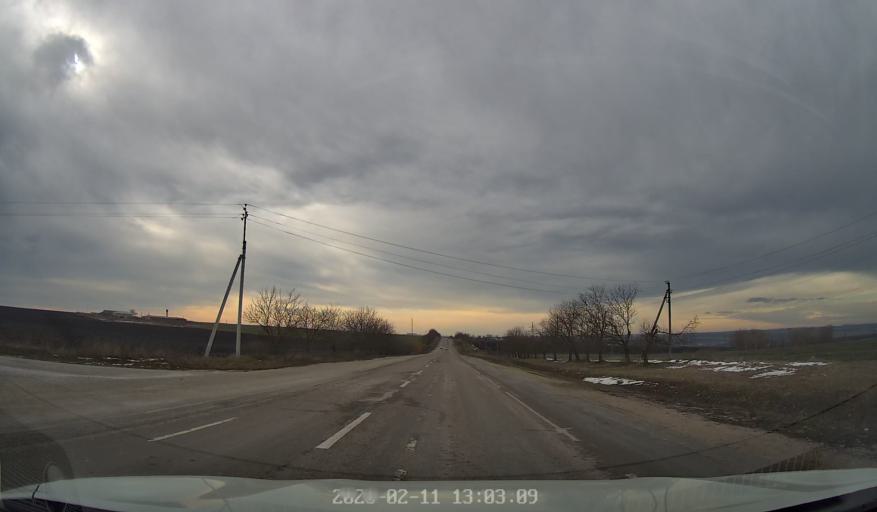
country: MD
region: Briceni
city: Briceni
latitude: 48.3145
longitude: 26.9655
